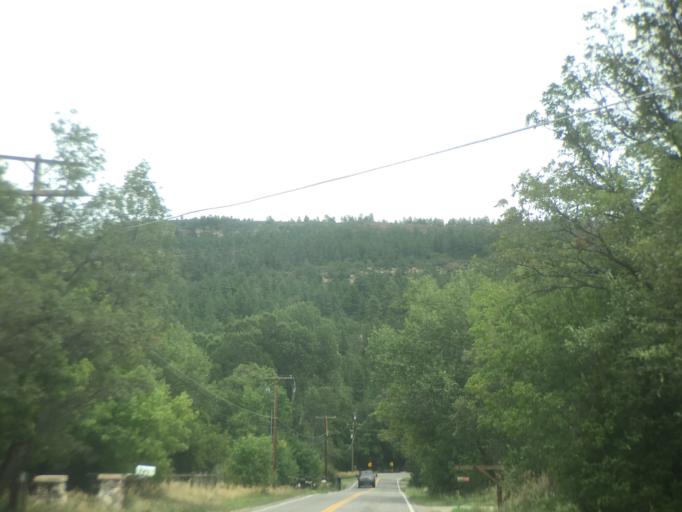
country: US
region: Colorado
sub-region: La Plata County
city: Durango
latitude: 37.3242
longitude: -107.8944
